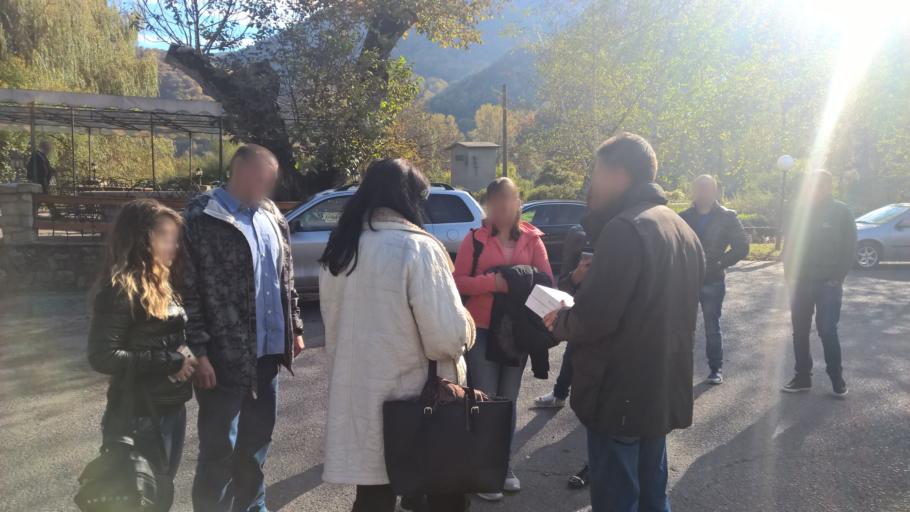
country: BG
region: Lovech
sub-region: Obshtina Teteven
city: Teteven
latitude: 42.9036
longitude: 24.3113
